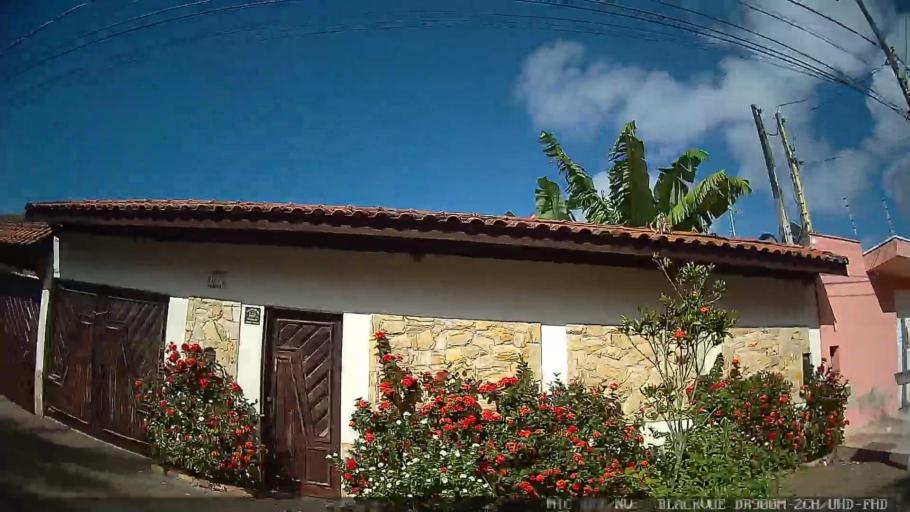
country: BR
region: Sao Paulo
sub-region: Peruibe
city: Peruibe
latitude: -24.2741
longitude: -46.9364
